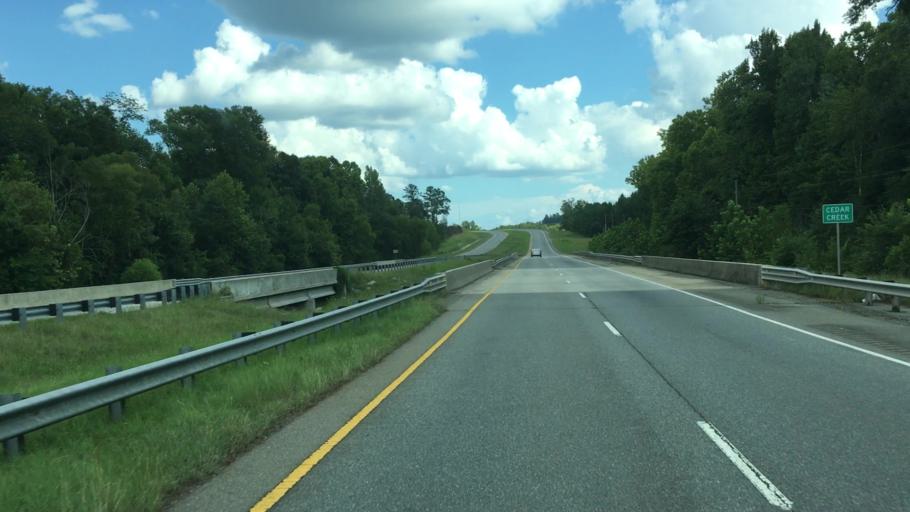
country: US
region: Georgia
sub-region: Wilkinson County
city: Irwinton
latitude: 32.7001
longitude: -83.1217
